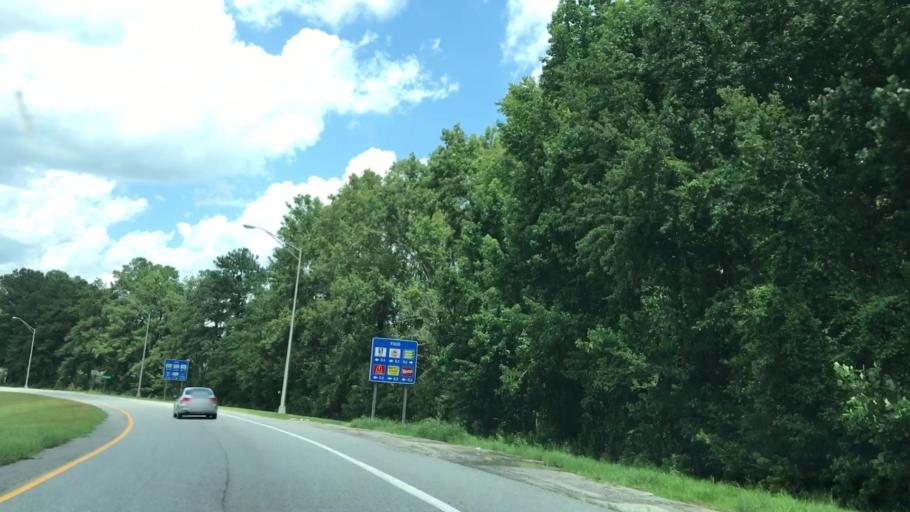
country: US
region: Georgia
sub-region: Bryan County
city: Richmond Hill
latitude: 31.9266
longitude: -81.3290
